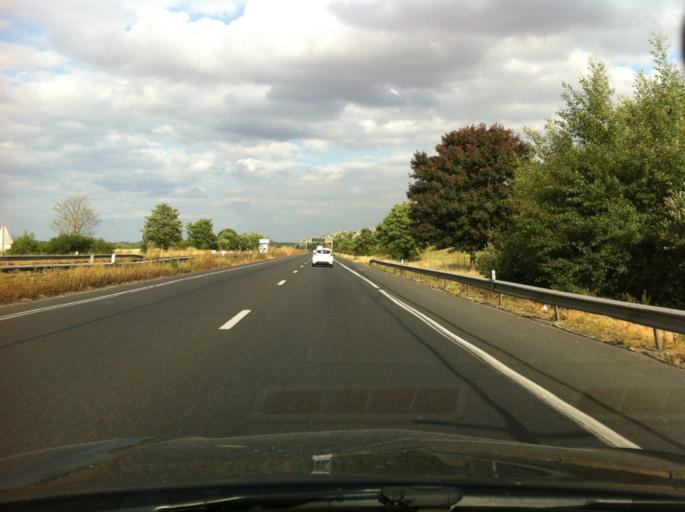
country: FR
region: Ile-de-France
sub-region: Departement de Seine-et-Marne
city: Moissy-Cramayel
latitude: 48.6464
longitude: 2.5925
